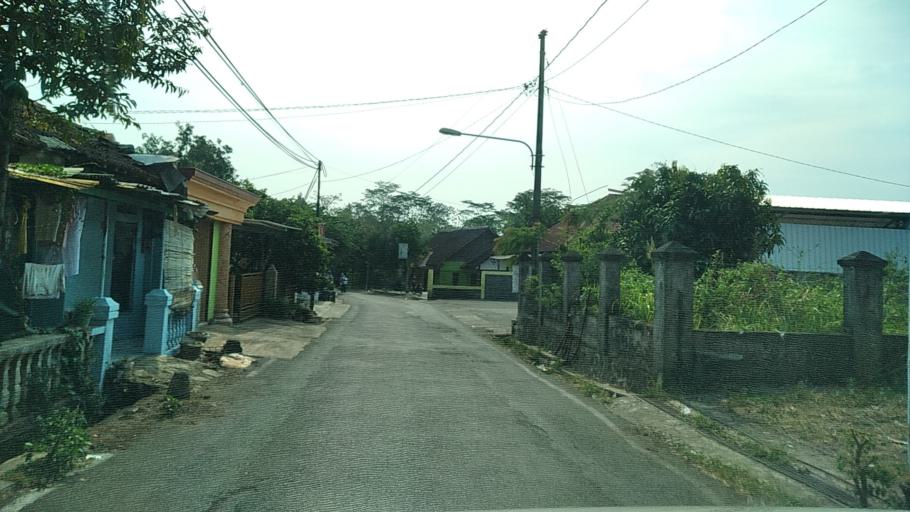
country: ID
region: Central Java
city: Semarang
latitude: -7.0544
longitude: 110.3146
